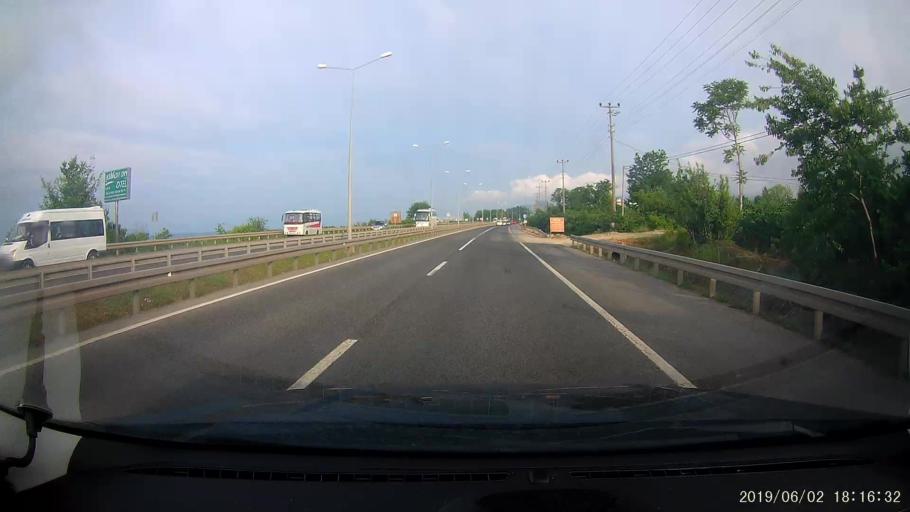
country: TR
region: Ordu
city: Unieh
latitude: 41.0994
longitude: 37.4002
